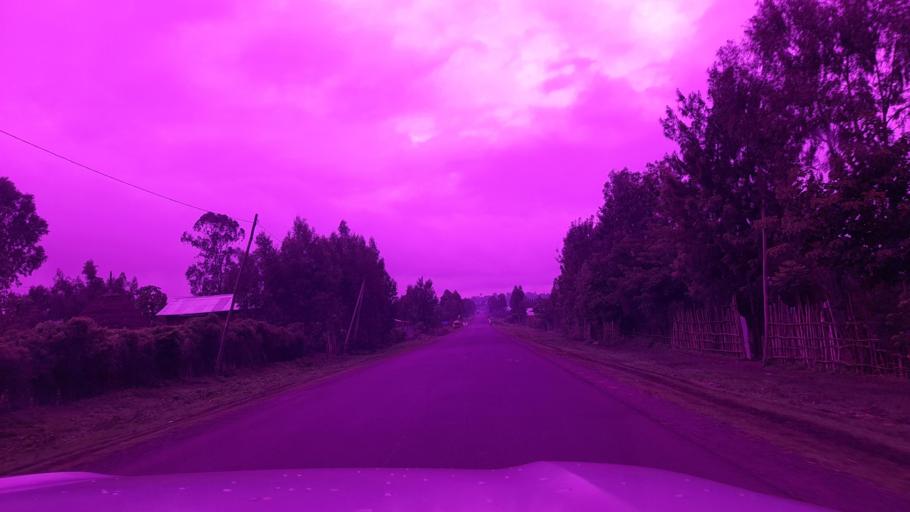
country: ET
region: Oromiya
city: Waliso
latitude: 8.2802
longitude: 37.6923
